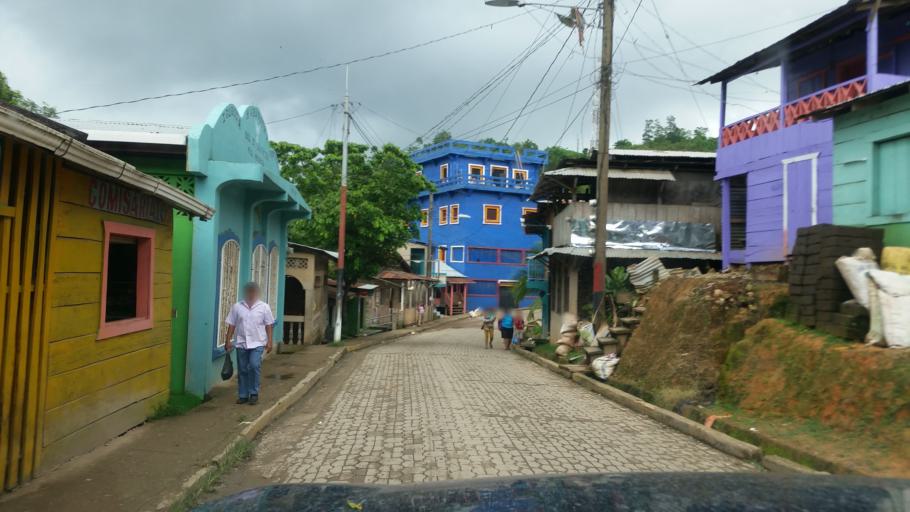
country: NI
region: Atlantico Norte (RAAN)
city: Bonanza
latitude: 14.0309
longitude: -84.6007
